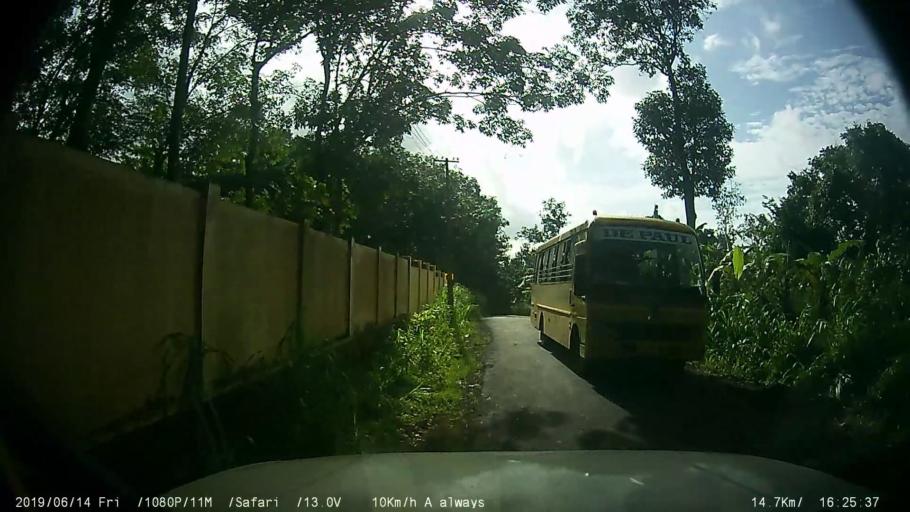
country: IN
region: Kerala
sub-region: Kottayam
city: Palackattumala
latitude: 9.7755
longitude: 76.5945
